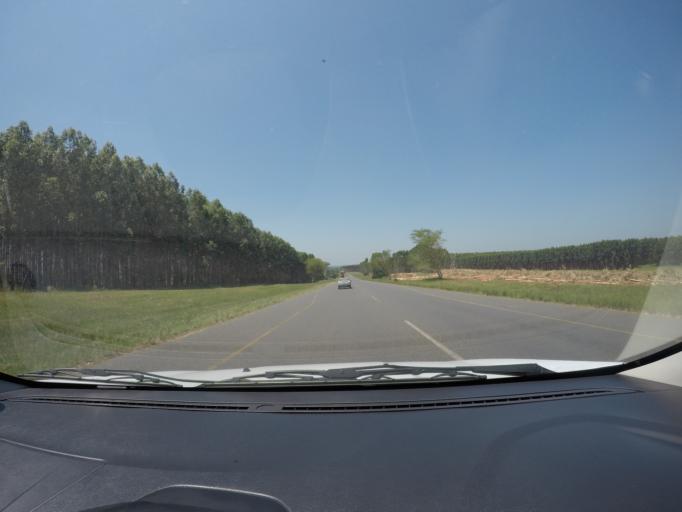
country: ZA
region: KwaZulu-Natal
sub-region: uThungulu District Municipality
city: eSikhawini
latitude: -28.8210
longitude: 31.9494
